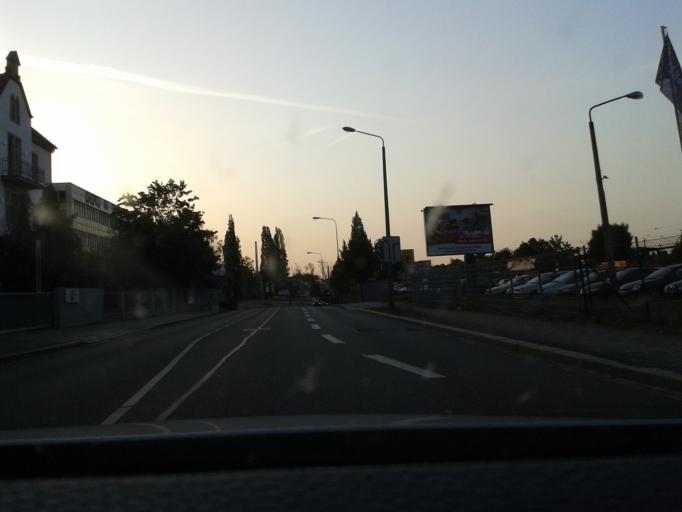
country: DE
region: Saxony
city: Heidenau
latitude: 51.0101
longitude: 13.8098
